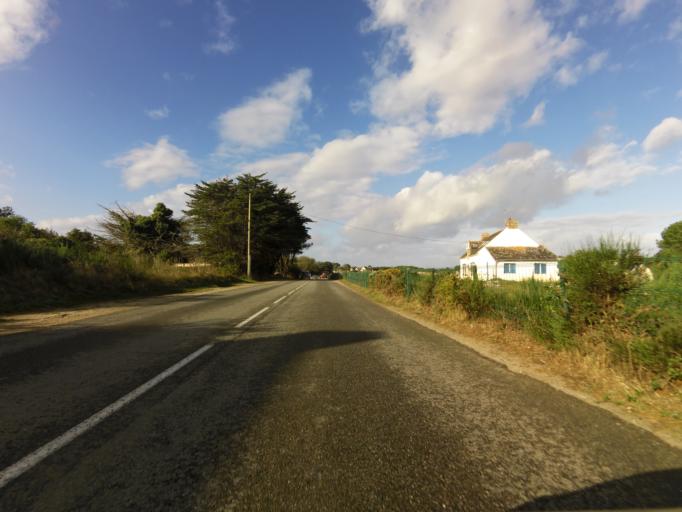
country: FR
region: Brittany
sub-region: Departement du Morbihan
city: Carnac
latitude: 47.5933
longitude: -3.0786
